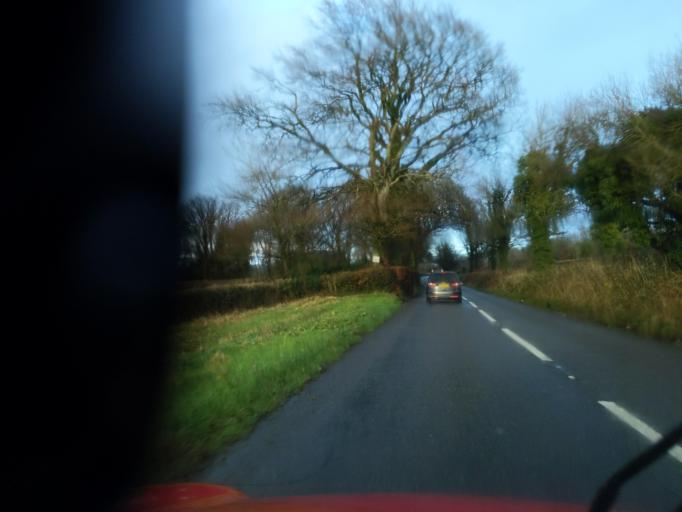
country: GB
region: England
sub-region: Devon
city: Okehampton
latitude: 50.6870
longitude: -4.0804
